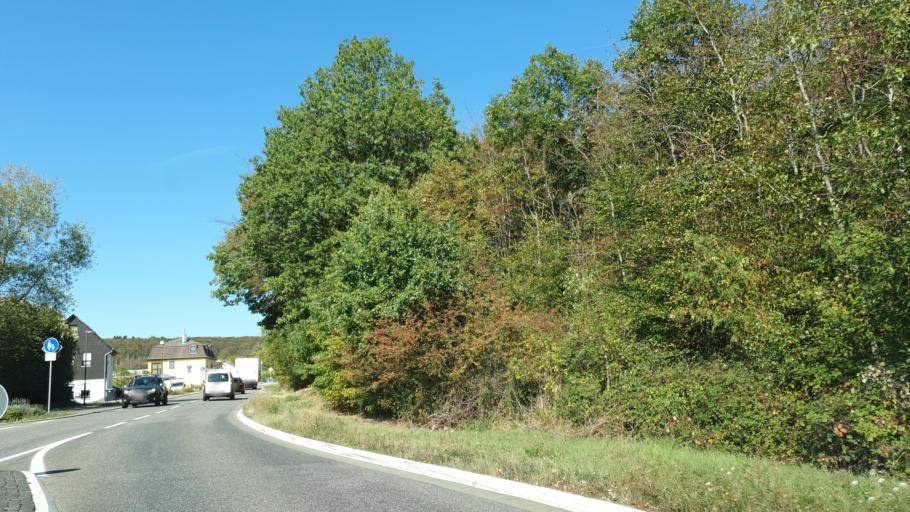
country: DE
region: Rheinland-Pfalz
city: Nortershausen
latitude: 50.2362
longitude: 7.5124
